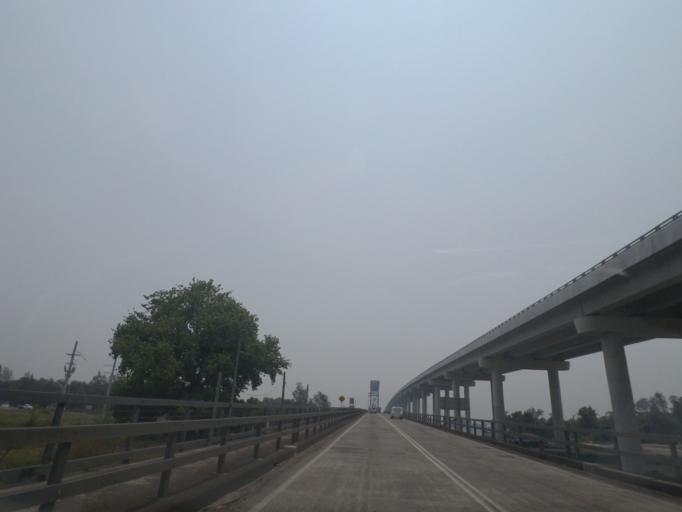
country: AU
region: New South Wales
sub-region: Clarence Valley
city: Maclean
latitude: -29.4342
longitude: 153.2407
